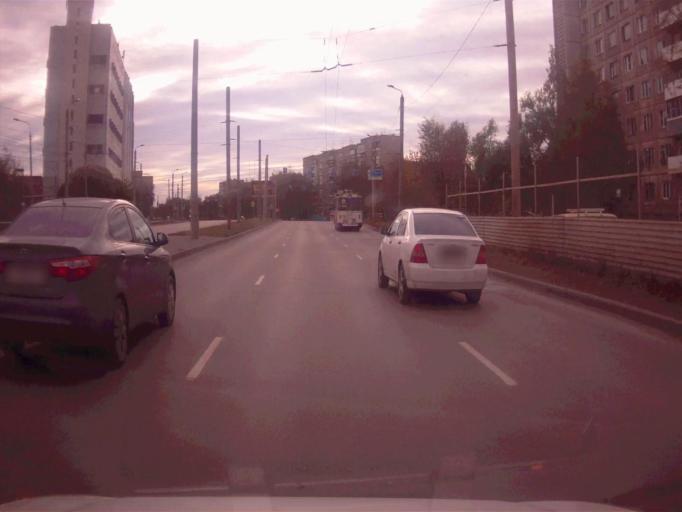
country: RU
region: Chelyabinsk
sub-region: Gorod Chelyabinsk
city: Chelyabinsk
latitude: 55.1267
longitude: 61.4776
